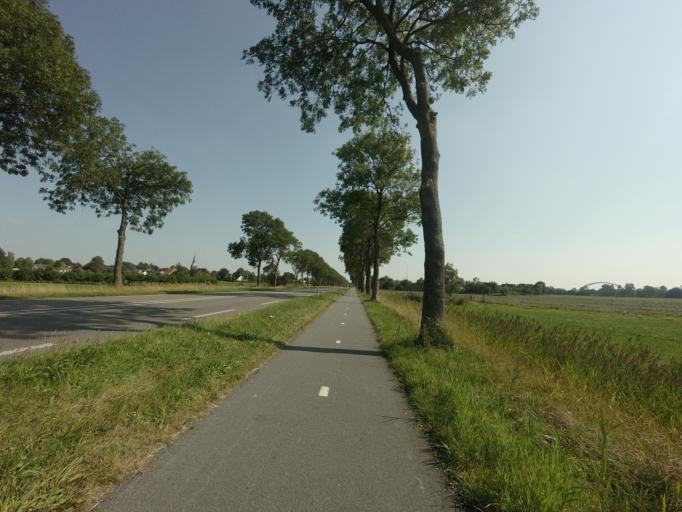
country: NL
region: Groningen
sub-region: Gemeente Zuidhorn
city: Noordhorn
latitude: 53.2619
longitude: 6.3890
